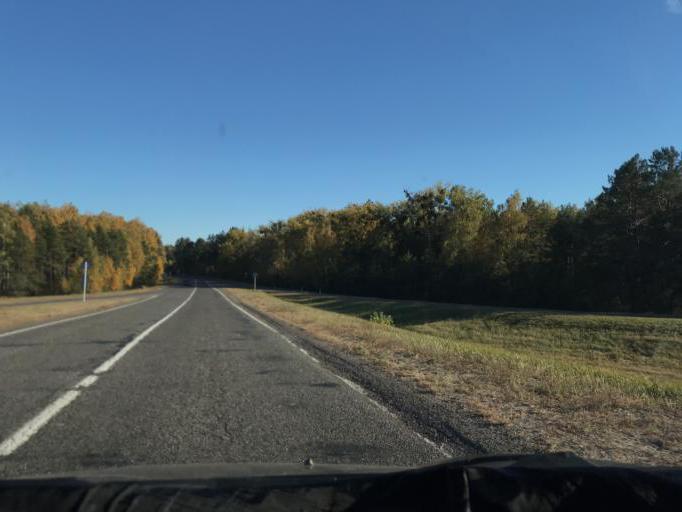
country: BY
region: Gomel
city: Kalinkavichy
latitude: 52.0724
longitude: 29.3630
